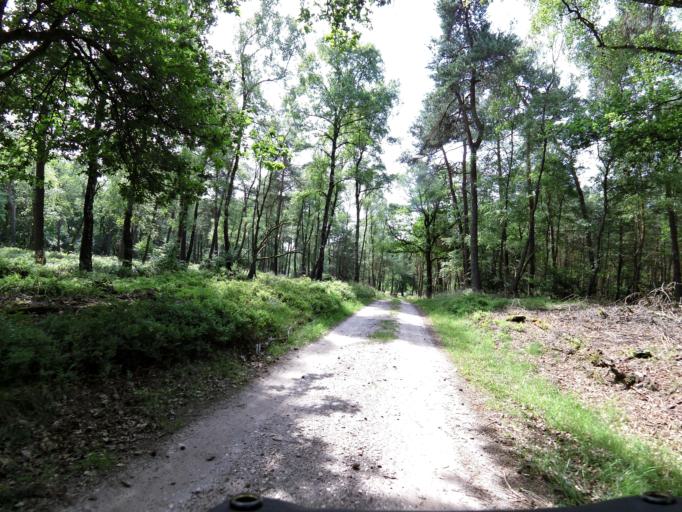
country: NL
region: Gelderland
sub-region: Gemeente Rozendaal
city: Rozendaal
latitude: 52.0655
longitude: 5.9801
